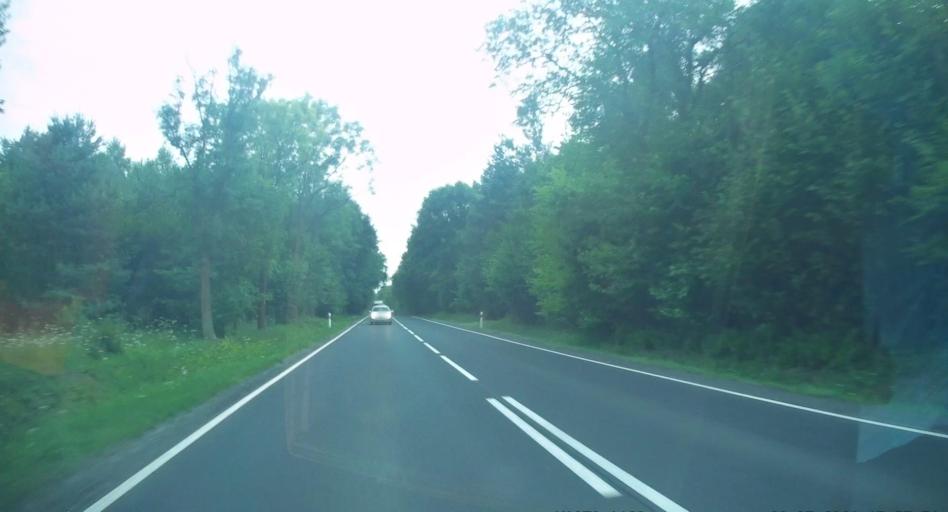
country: PL
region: Lodz Voivodeship
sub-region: Powiat radomszczanski
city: Gomunice
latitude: 51.1770
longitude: 19.4950
